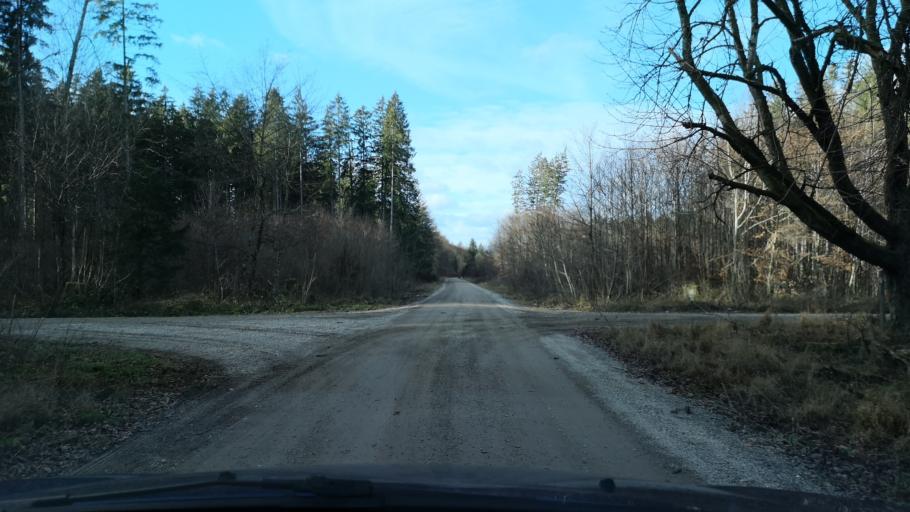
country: DE
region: Bavaria
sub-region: Upper Bavaria
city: Kirchseeon
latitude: 48.1103
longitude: 11.9223
